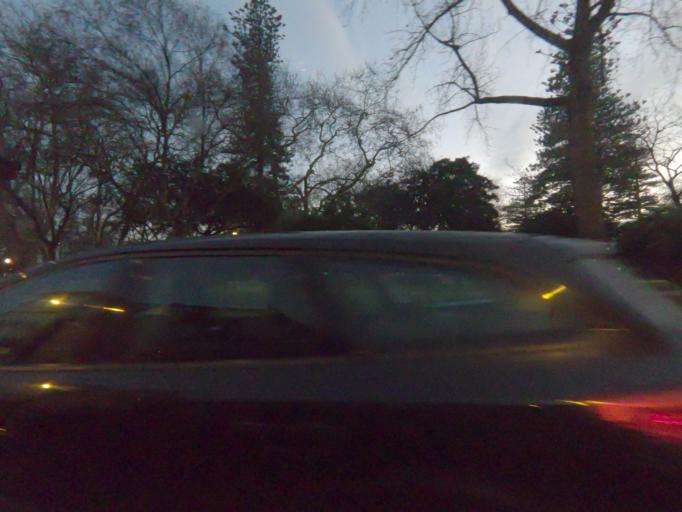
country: PT
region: Porto
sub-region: Vila Nova de Gaia
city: Canidelo
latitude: 41.1490
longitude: -8.6714
